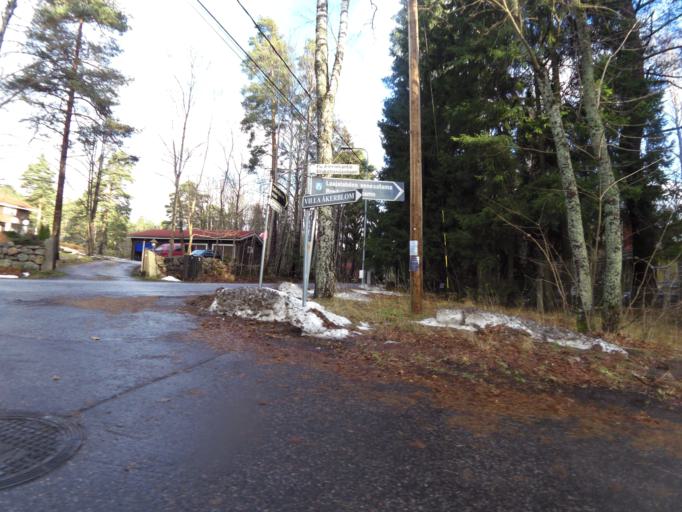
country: FI
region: Uusimaa
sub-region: Helsinki
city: Teekkarikylae
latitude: 60.2068
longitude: 24.8206
